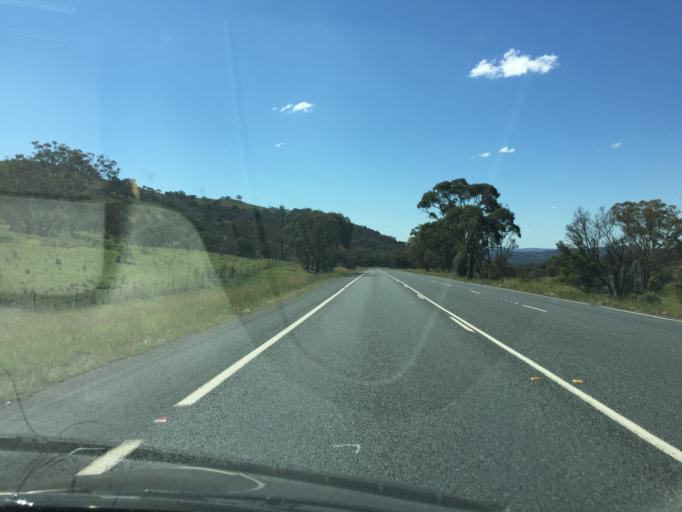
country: AU
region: Australian Capital Territory
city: Macarthur
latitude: -35.4740
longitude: 149.1412
